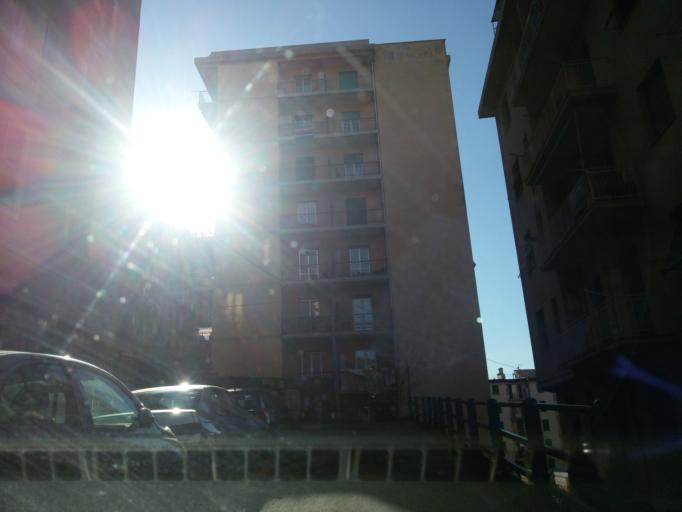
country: IT
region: Liguria
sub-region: Provincia di Genova
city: Genoa
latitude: 44.4154
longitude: 8.9602
